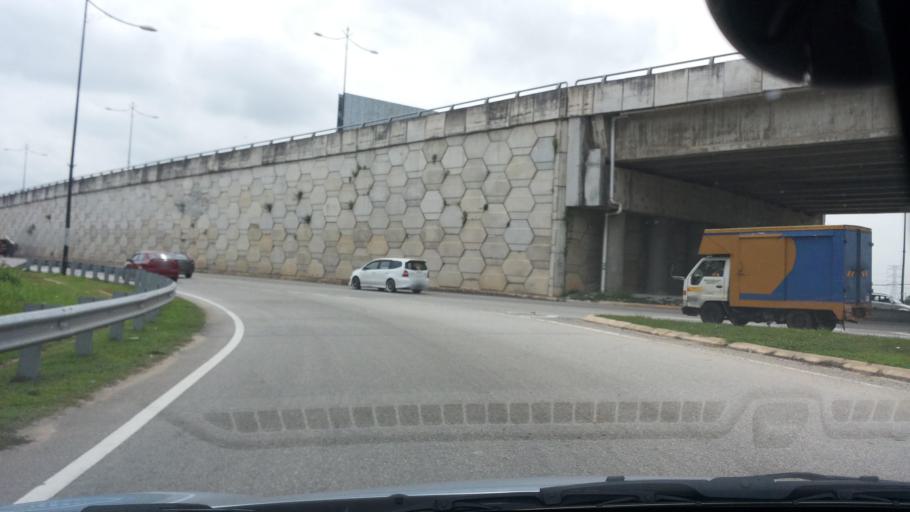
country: MY
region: Pahang
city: Kuantan
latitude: 3.7717
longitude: 103.2580
